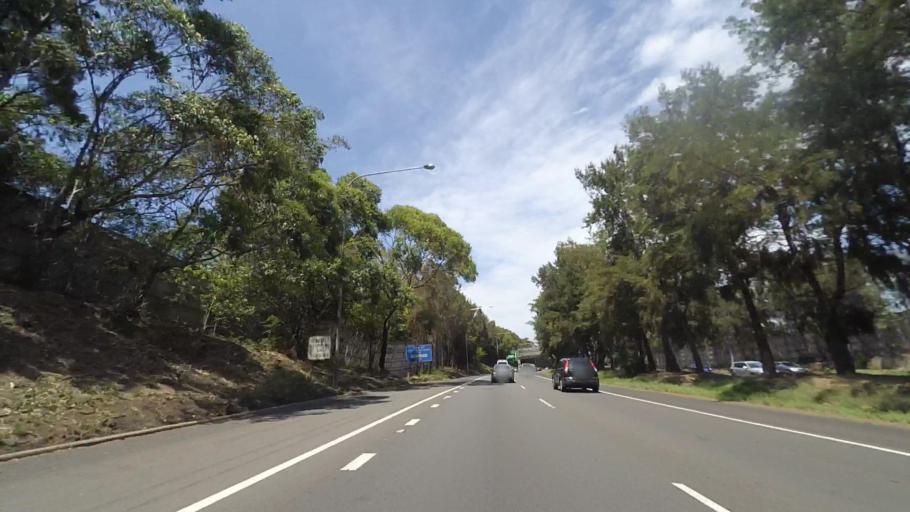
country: AU
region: New South Wales
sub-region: Wollongong
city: Mangerton
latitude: -34.4333
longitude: 150.8685
